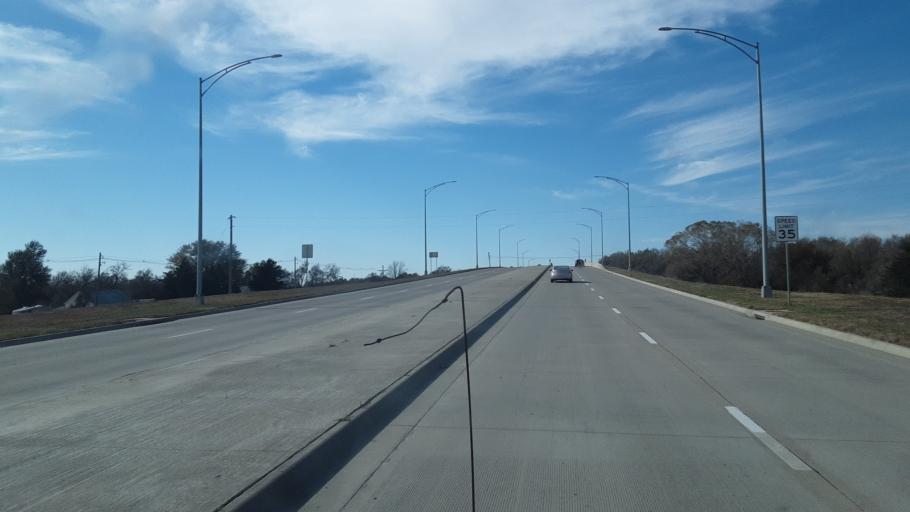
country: US
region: Kansas
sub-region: McPherson County
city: McPherson
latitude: 38.3701
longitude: -97.6356
